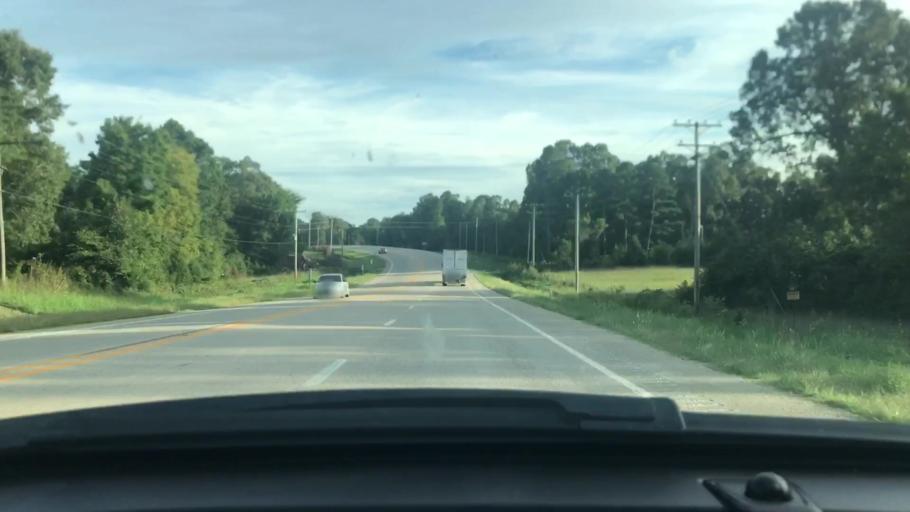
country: US
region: Arkansas
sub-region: Lawrence County
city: Hoxie
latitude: 36.1328
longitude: -91.1583
